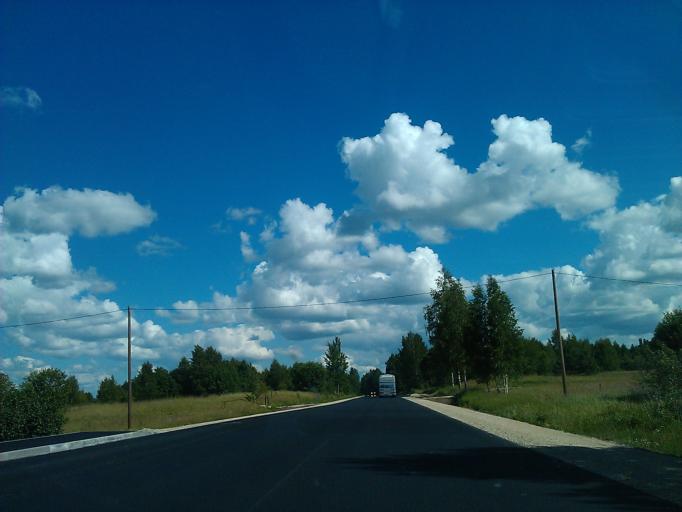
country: LV
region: Vilanu
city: Vilani
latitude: 56.5509
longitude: 27.0969
